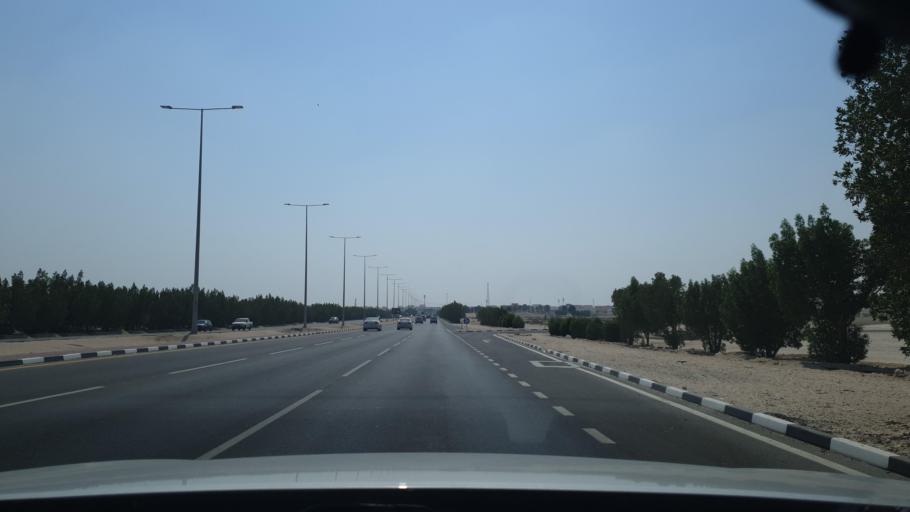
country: QA
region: Al Khawr
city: Al Khawr
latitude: 25.6995
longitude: 51.5027
